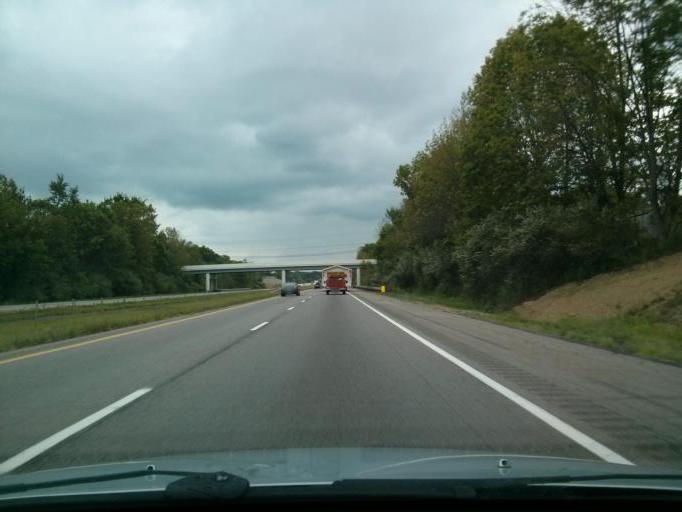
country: US
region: Ohio
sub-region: Mahoning County
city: Craig Beach
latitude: 41.0999
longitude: -80.9913
